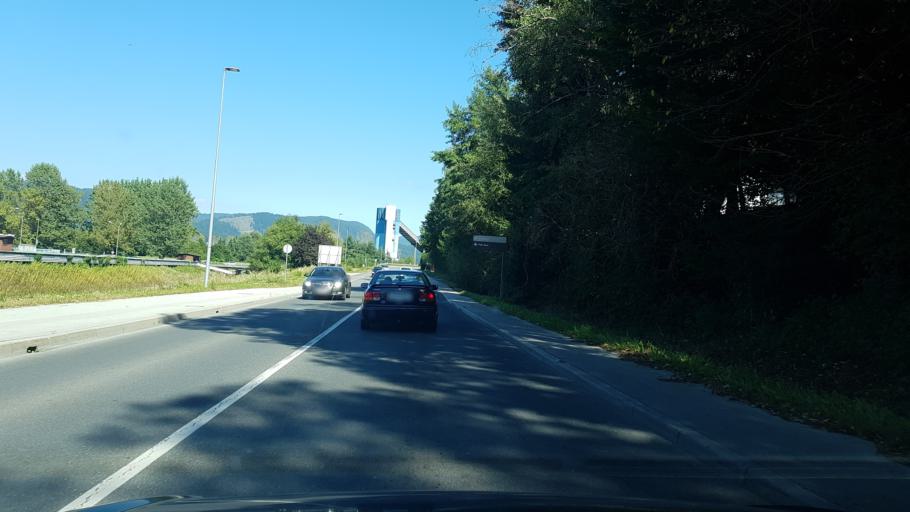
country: SI
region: Sostanj
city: Sostanj
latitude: 46.3683
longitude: 15.0709
